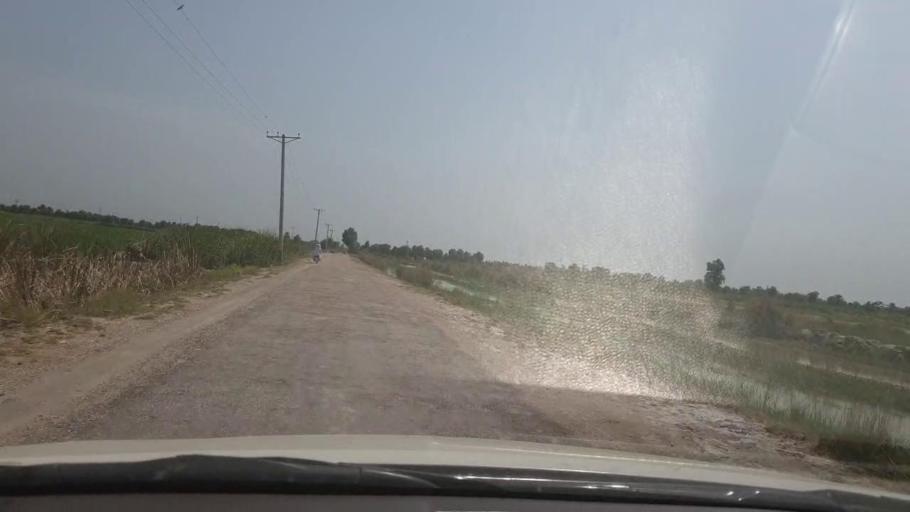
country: PK
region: Sindh
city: Garhi Yasin
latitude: 27.9801
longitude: 68.5027
